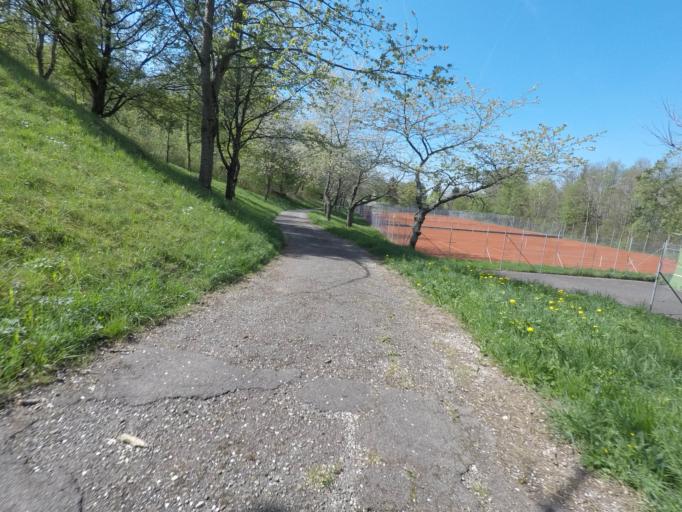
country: DE
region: Baden-Wuerttemberg
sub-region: Tuebingen Region
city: Pfullingen
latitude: 48.4496
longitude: 9.2311
